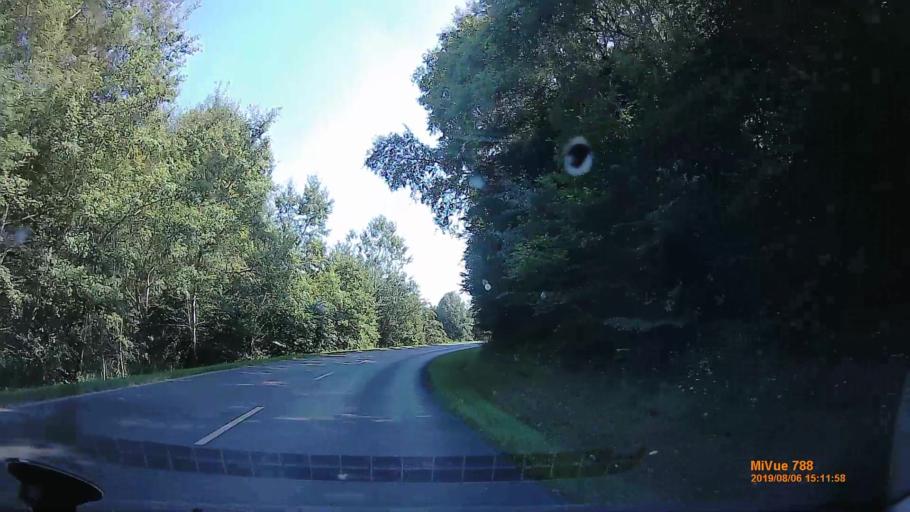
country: HU
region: Zala
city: Nagykanizsa
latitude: 46.3714
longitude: 16.9777
